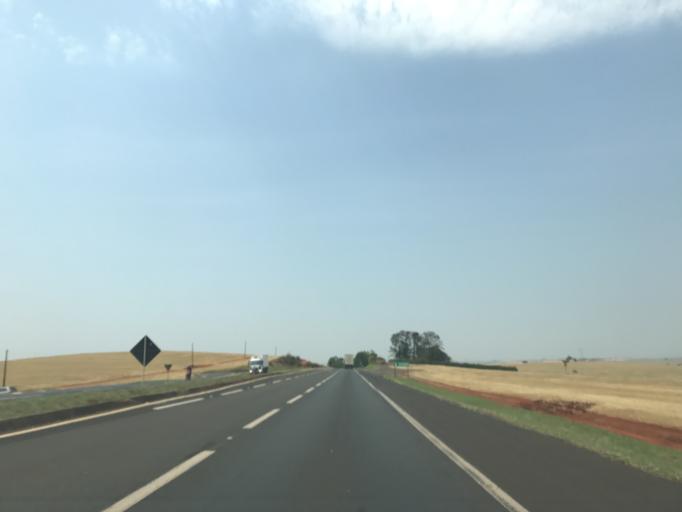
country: BR
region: Parana
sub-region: Rolandia
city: Rolandia
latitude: -23.3395
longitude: -51.3644
